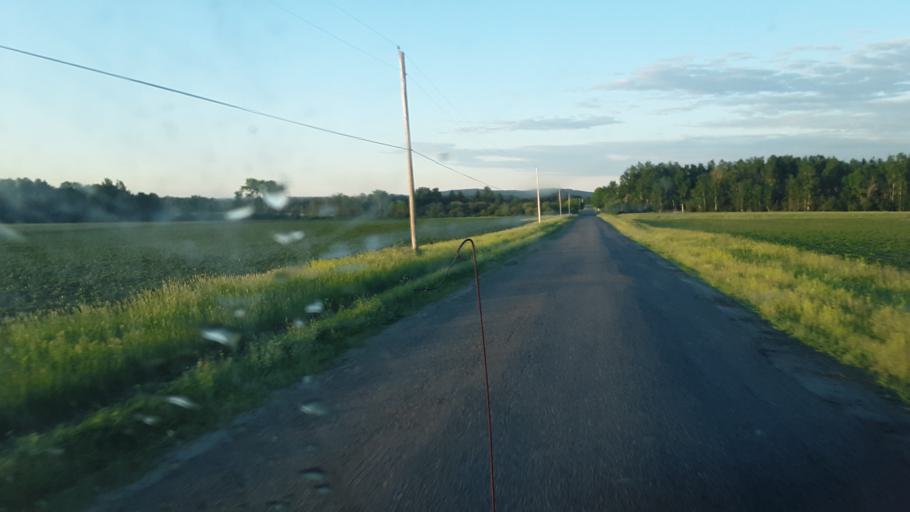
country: US
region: Maine
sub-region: Aroostook County
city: Caribou
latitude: 46.7988
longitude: -68.0978
